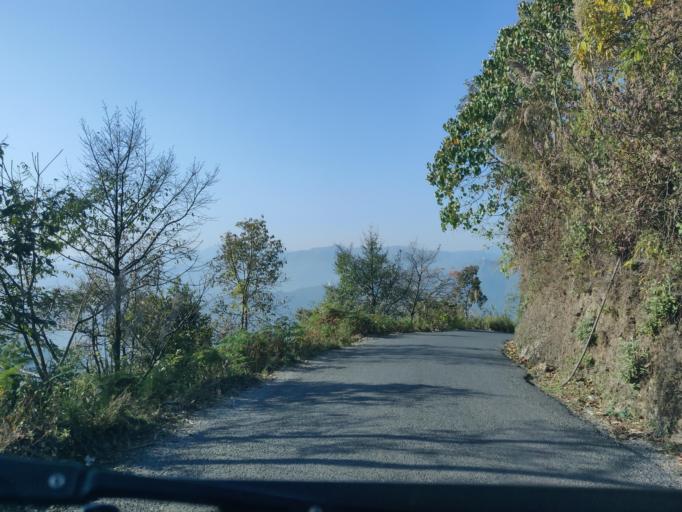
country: NP
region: Western Region
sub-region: Gandaki Zone
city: Pokhara
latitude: 28.2438
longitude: 83.9579
